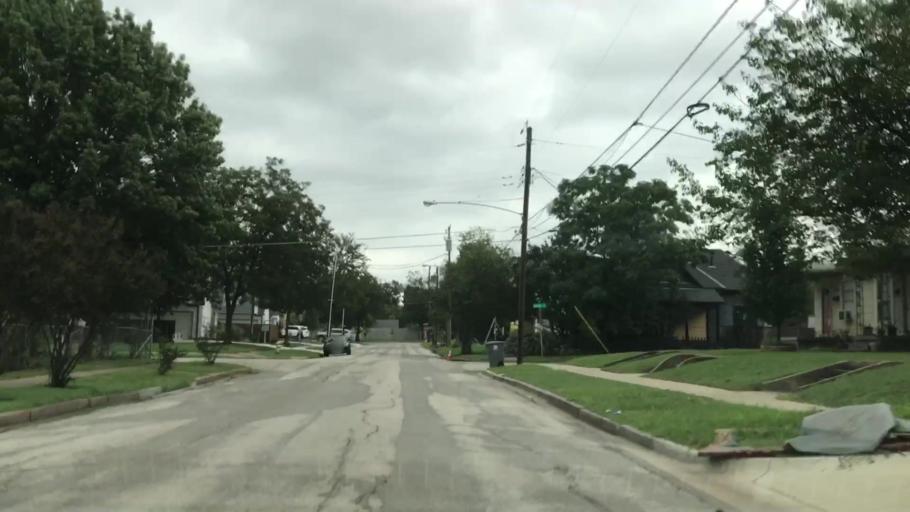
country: US
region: Texas
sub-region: Dallas County
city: Dallas
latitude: 32.8033
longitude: -96.7833
